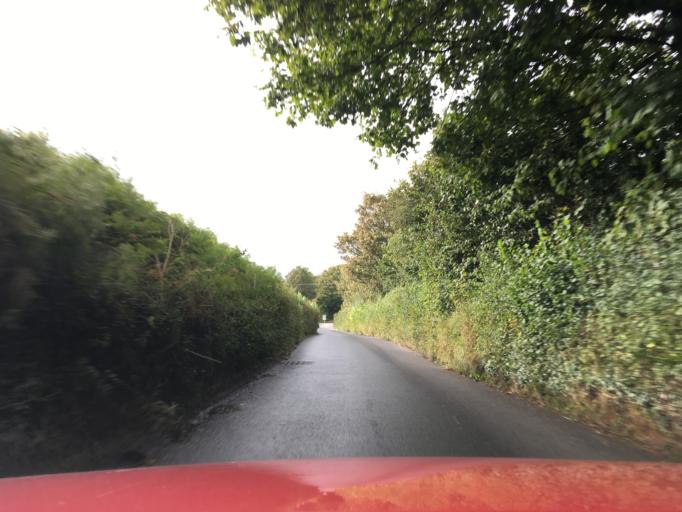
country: GB
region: England
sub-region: Devon
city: Ivybridge
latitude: 50.3521
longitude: -3.9265
